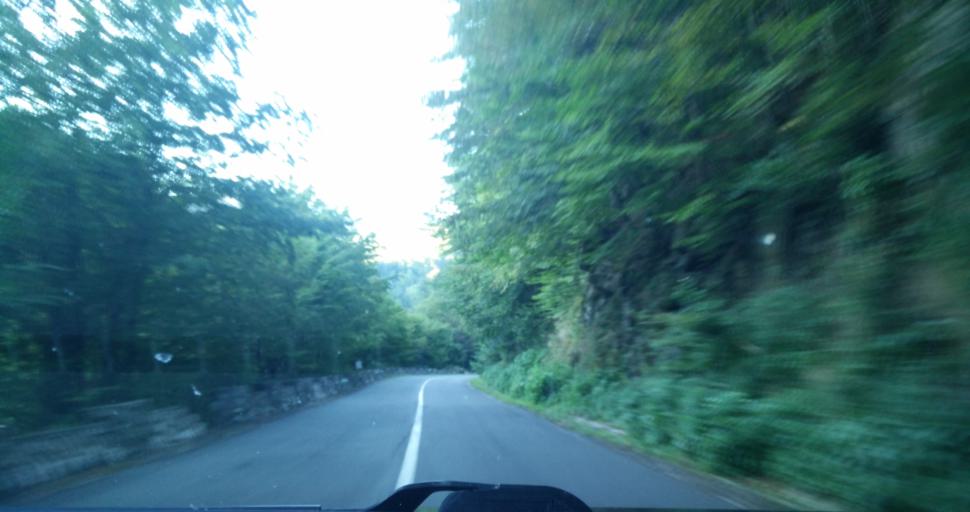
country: RO
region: Bihor
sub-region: Oras Nucet
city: Nucet
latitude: 46.4838
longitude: 22.5978
